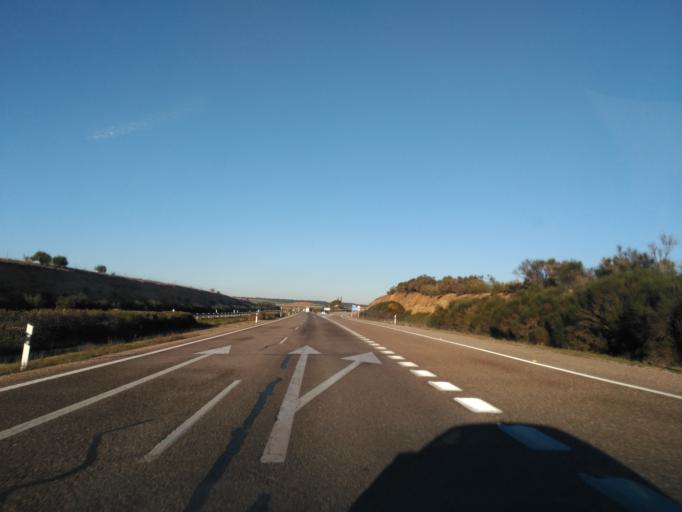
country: ES
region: Castille and Leon
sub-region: Provincia de Salamanca
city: Parada de Rubiales
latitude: 41.1534
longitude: -5.4563
